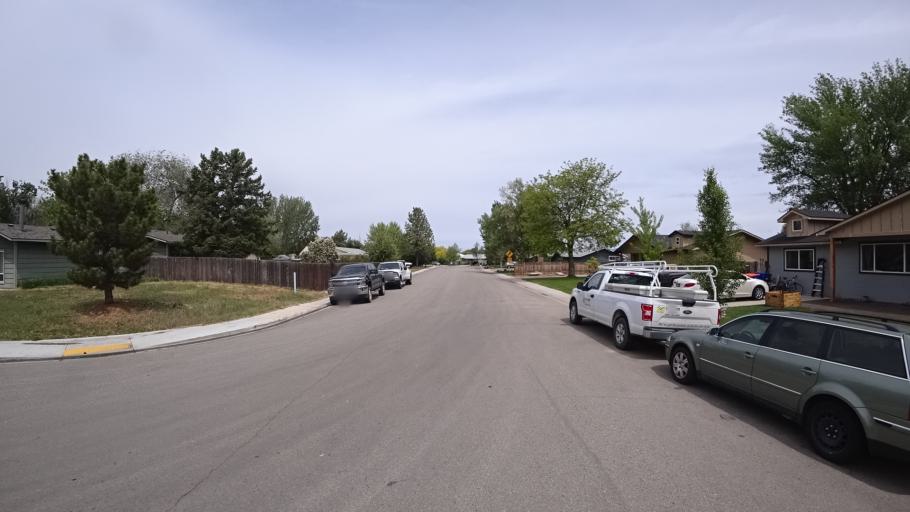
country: US
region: Idaho
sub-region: Ada County
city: Meridian
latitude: 43.5429
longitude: -116.3252
